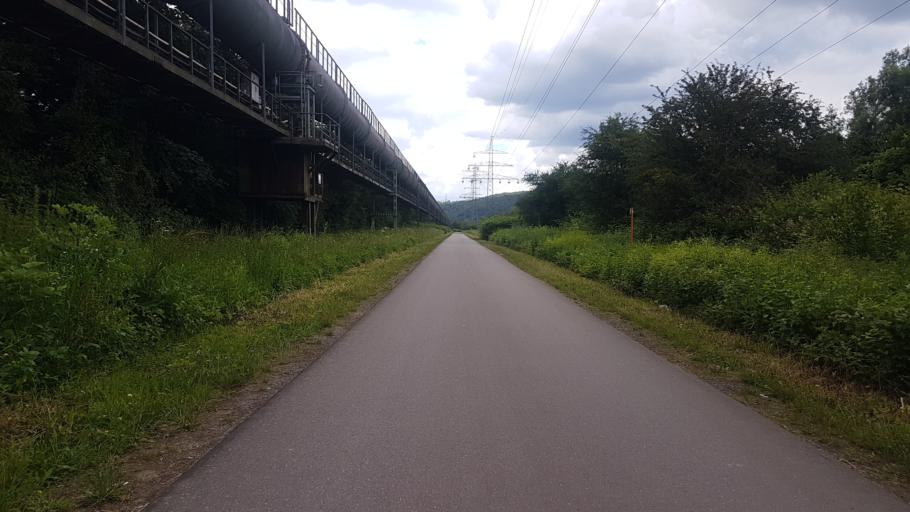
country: DE
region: Saarland
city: Volklingen
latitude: 49.2543
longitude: 6.8390
